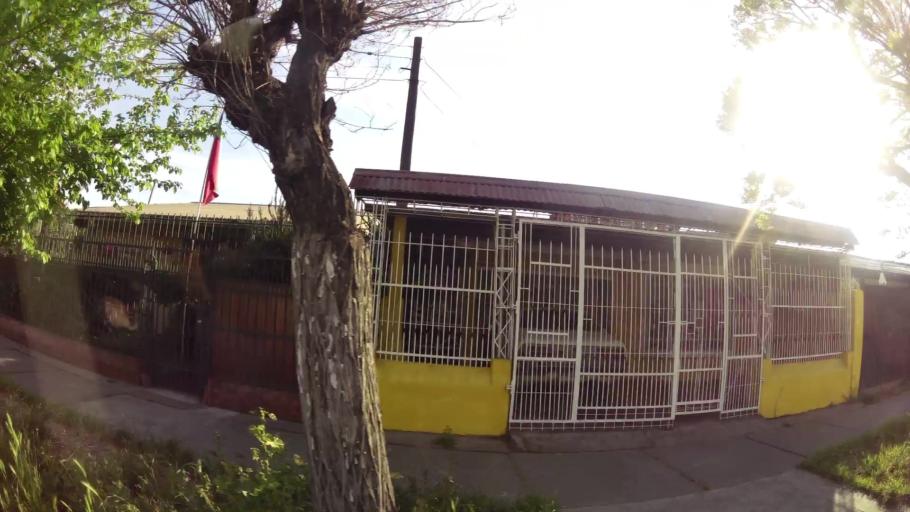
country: CL
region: Santiago Metropolitan
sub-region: Provincia de Santiago
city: Santiago
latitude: -33.5107
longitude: -70.6675
